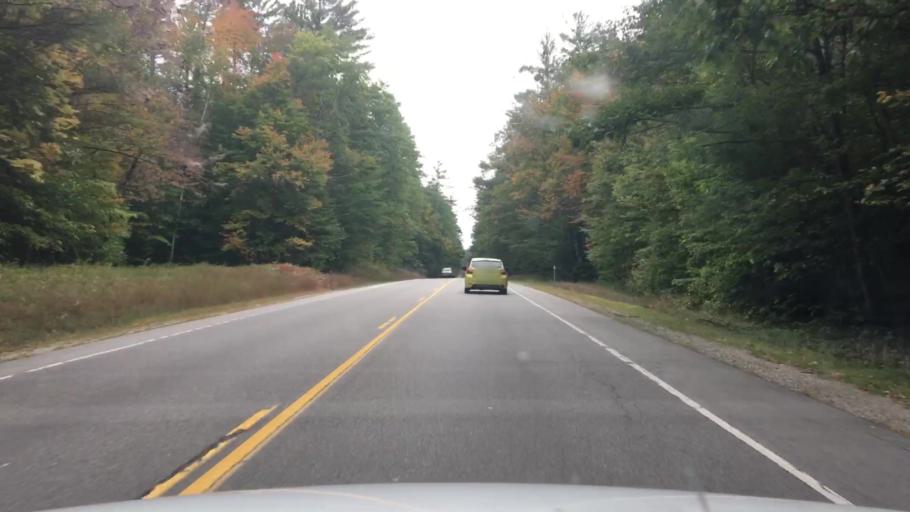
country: US
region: New Hampshire
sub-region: Carroll County
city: Tamworth
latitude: 43.9046
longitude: -71.2324
